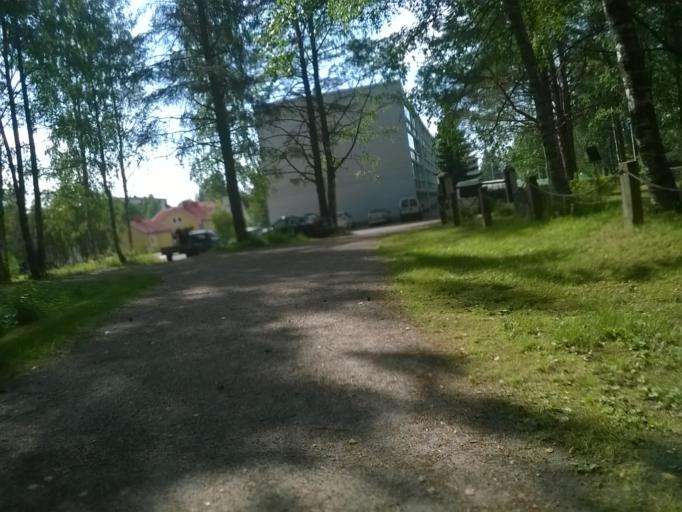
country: FI
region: Kainuu
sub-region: Kehys-Kainuu
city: Kuhmo
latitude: 64.1311
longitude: 29.5238
